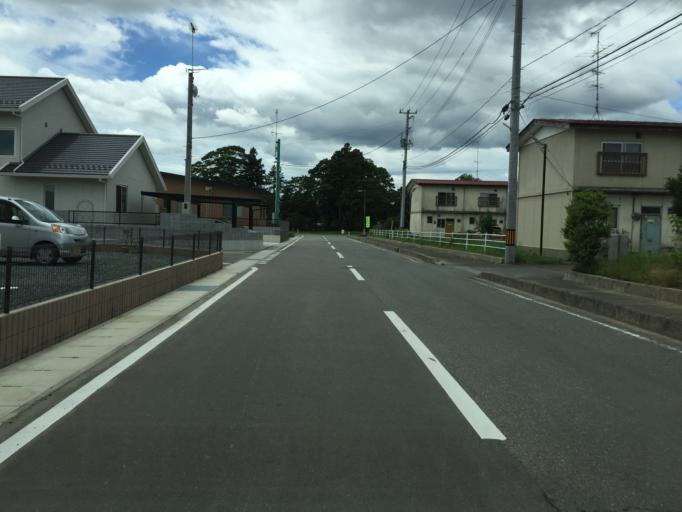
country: JP
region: Fukushima
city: Namie
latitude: 37.7007
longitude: 140.9774
